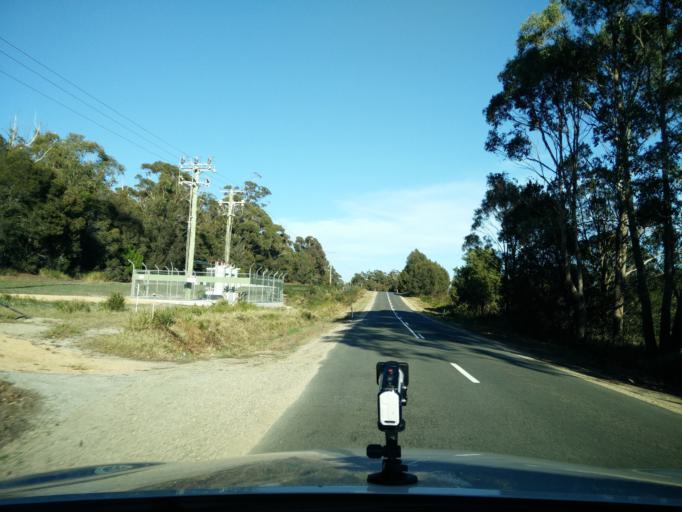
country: AU
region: Tasmania
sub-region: Break O'Day
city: St Helens
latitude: -41.2965
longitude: 148.1980
